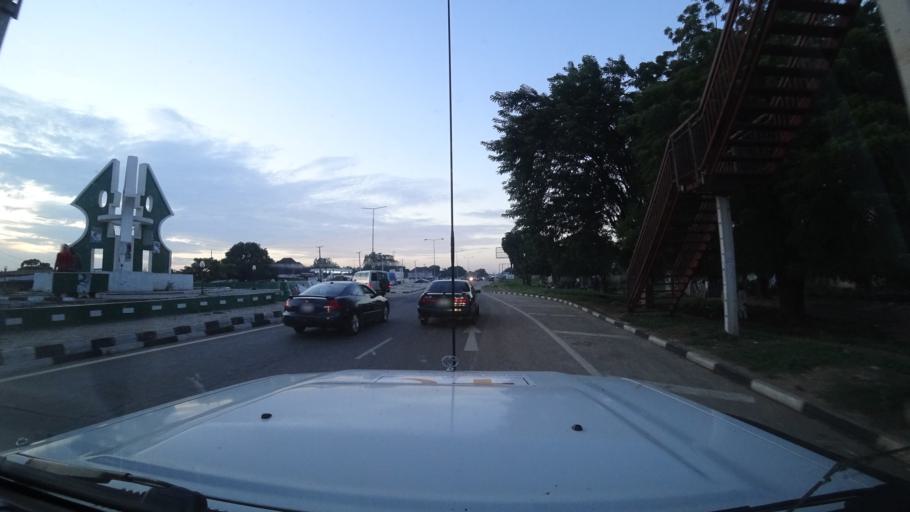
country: NG
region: Niger
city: Minna
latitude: 9.6400
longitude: 6.5415
